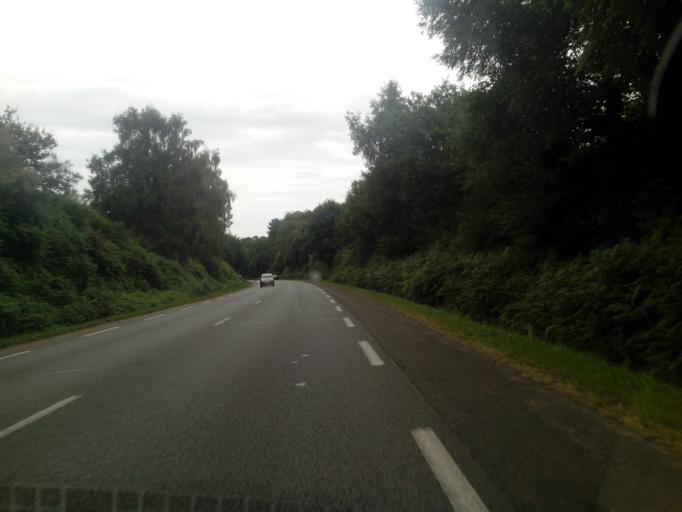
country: FR
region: Brittany
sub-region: Departement du Morbihan
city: Hennebont
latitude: 47.7777
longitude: -3.2743
